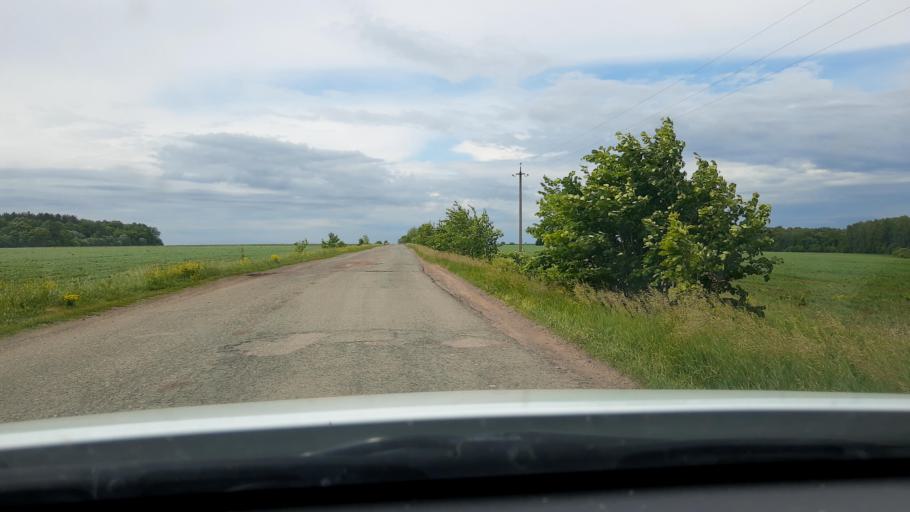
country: RU
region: Bashkortostan
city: Iglino
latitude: 54.7438
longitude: 56.5346
